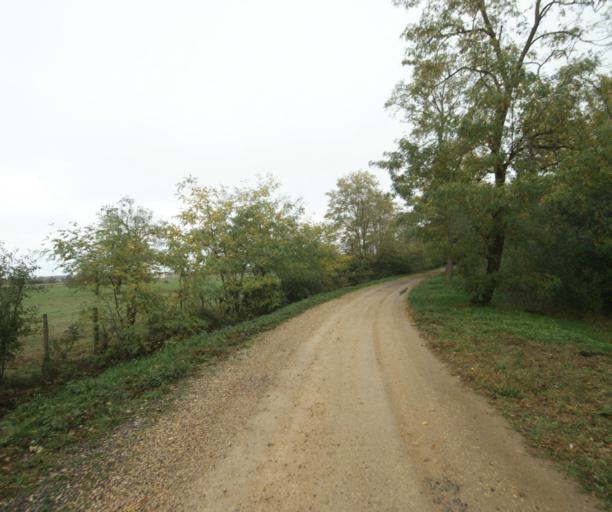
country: FR
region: Rhone-Alpes
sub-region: Departement de l'Ain
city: Pont-de-Vaux
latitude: 46.4569
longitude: 4.8959
